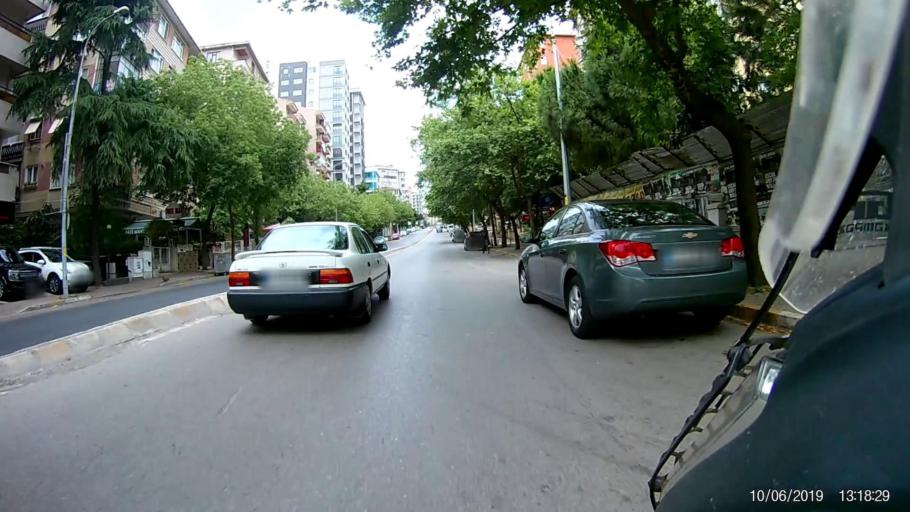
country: TR
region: Istanbul
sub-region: Atasehir
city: Atasehir
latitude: 40.9567
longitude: 29.1010
